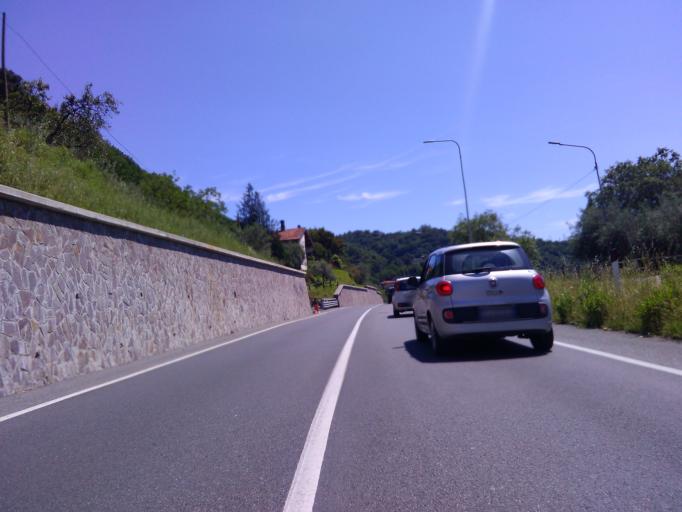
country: IT
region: Tuscany
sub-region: Provincia di Massa-Carrara
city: Albiano Magra
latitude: 44.1824
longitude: 9.9268
